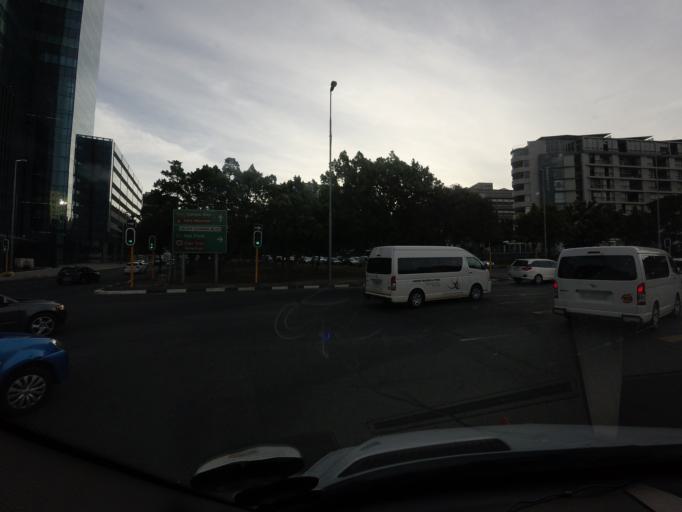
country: ZA
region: Western Cape
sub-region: City of Cape Town
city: Cape Town
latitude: -33.9159
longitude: 18.4223
